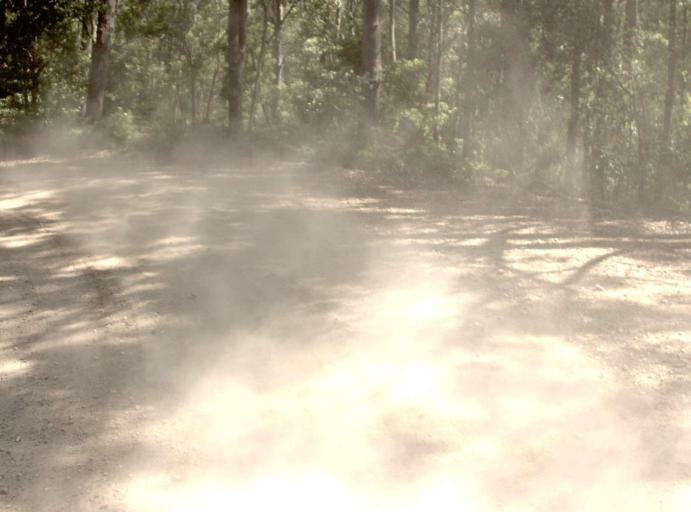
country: AU
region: Victoria
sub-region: East Gippsland
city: Lakes Entrance
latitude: -37.6106
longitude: 148.7072
